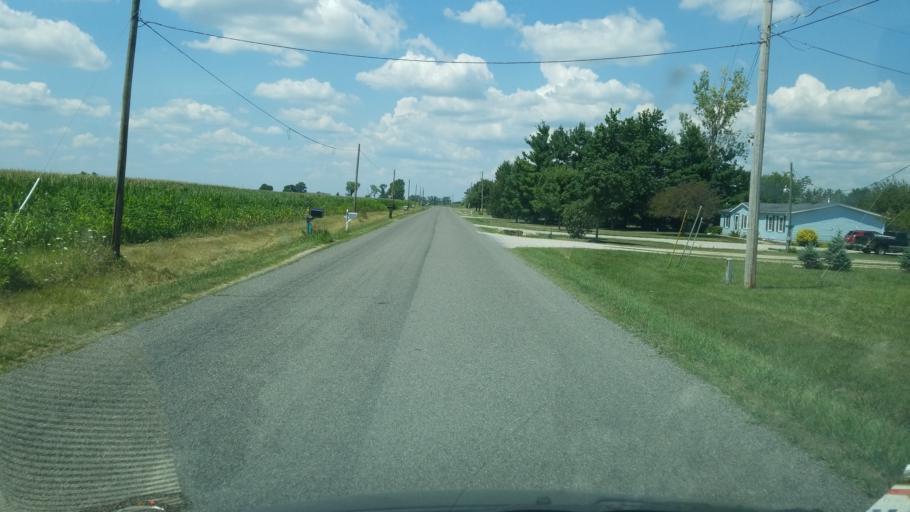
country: US
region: Ohio
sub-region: Champaign County
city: Mechanicsburg
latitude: 40.0832
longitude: -83.4594
